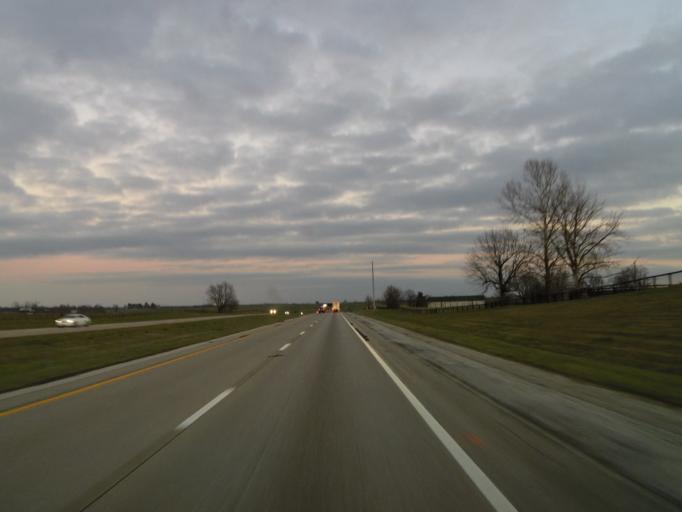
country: US
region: Kentucky
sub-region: Woodford County
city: Midway
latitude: 38.1618
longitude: -84.7167
